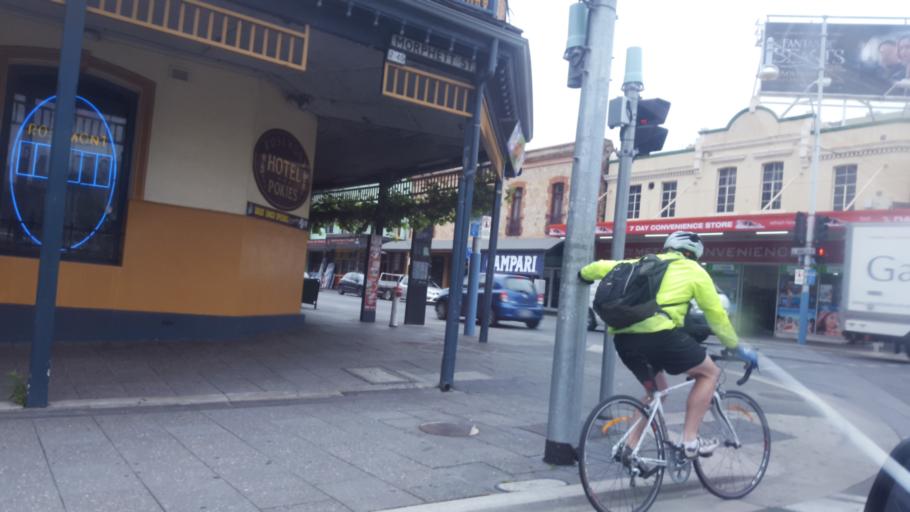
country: AU
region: South Australia
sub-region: Adelaide
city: Adelaide
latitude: -34.9231
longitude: 138.5936
